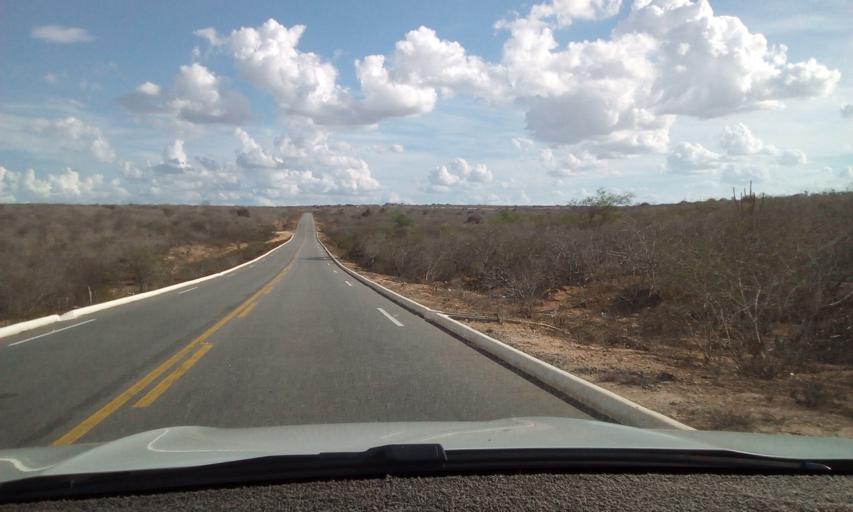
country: BR
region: Paraiba
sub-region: Soledade
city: Soledade
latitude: -6.8672
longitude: -36.4020
